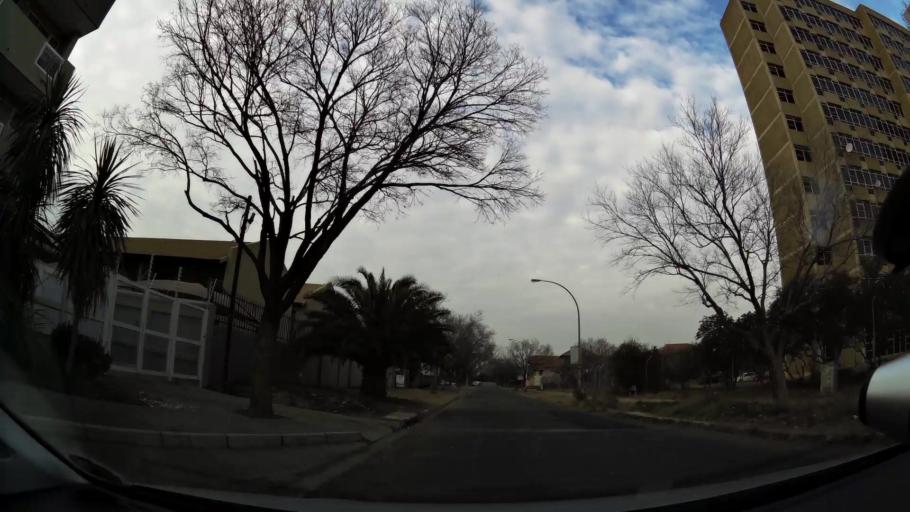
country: ZA
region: Orange Free State
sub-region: Mangaung Metropolitan Municipality
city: Bloemfontein
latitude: -29.1167
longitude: 26.1872
